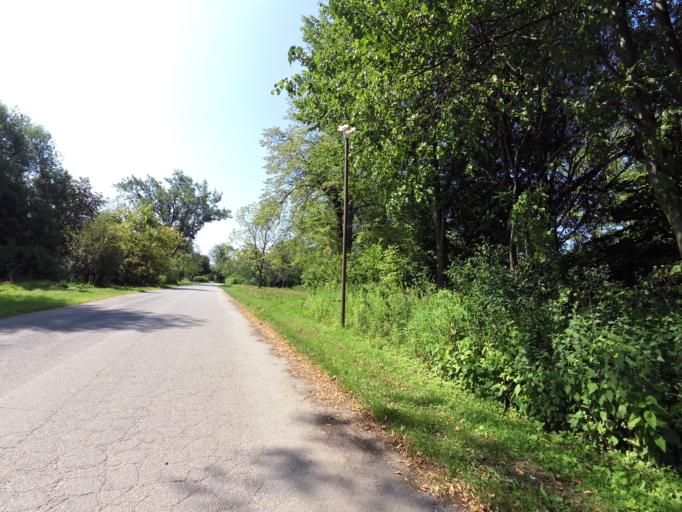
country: CA
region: Ontario
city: Toronto
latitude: 43.6239
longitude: -79.3902
